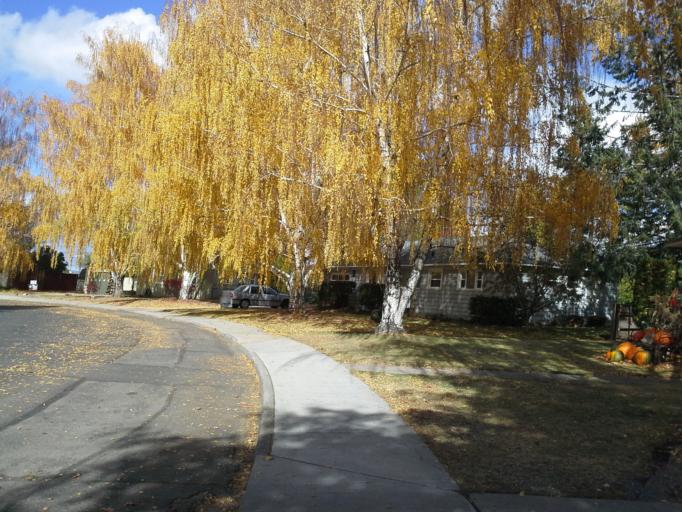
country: US
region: Oregon
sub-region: Baker County
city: Baker City
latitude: 44.7874
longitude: -117.8315
